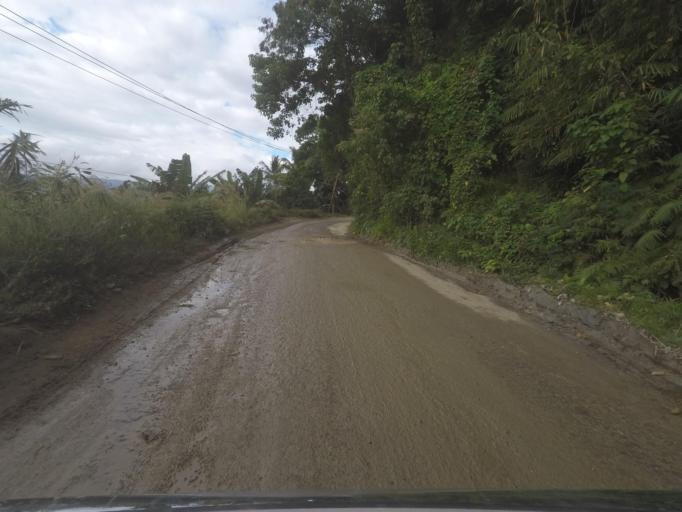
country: TL
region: Baucau
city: Venilale
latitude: -8.6024
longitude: 126.3842
